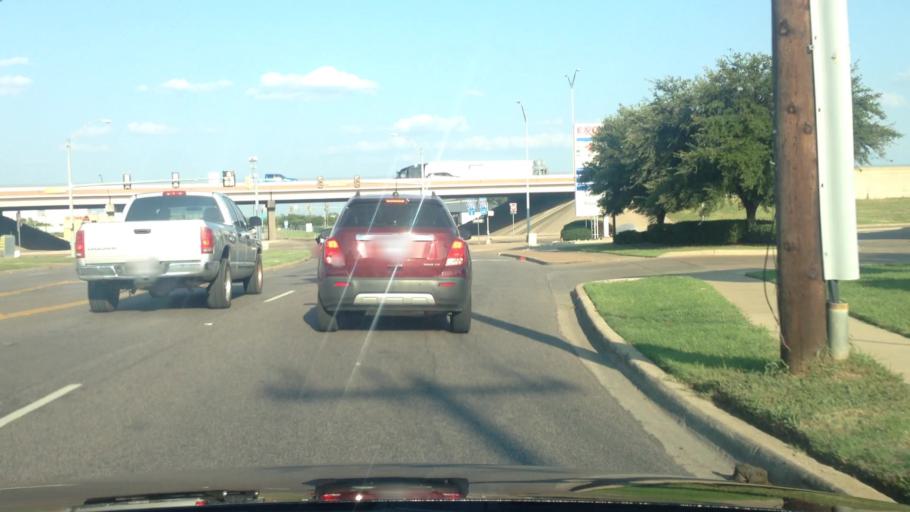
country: US
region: Texas
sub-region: Tarrant County
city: Edgecliff Village
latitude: 32.6350
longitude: -97.3230
